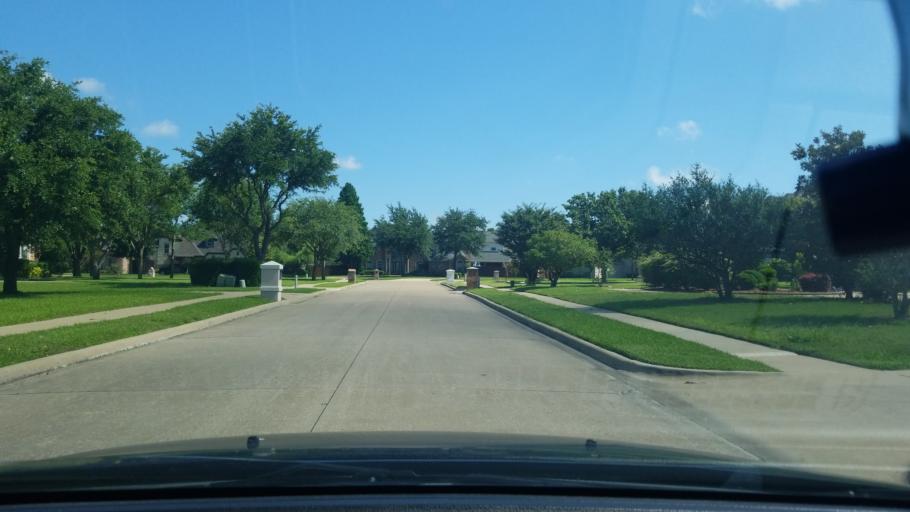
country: US
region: Texas
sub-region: Dallas County
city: Sunnyvale
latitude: 32.7922
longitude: -96.5738
